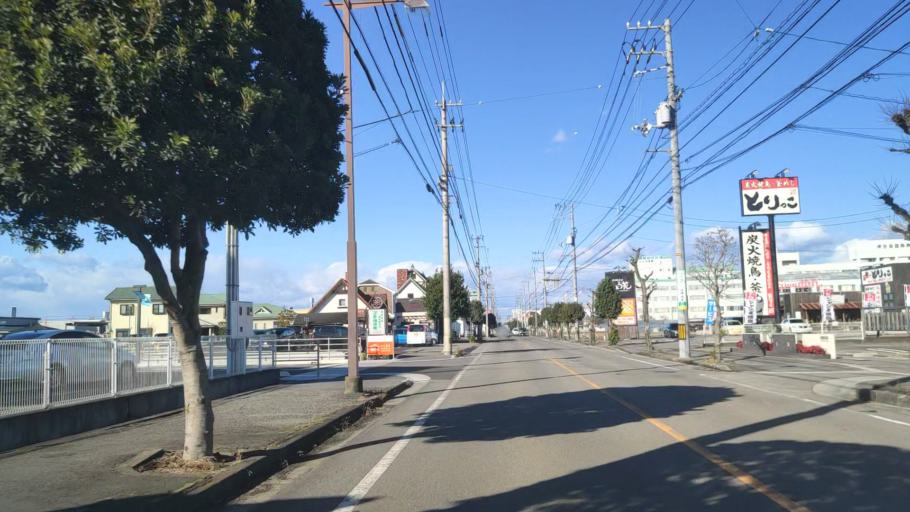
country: JP
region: Ehime
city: Saijo
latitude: 33.9264
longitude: 133.1908
